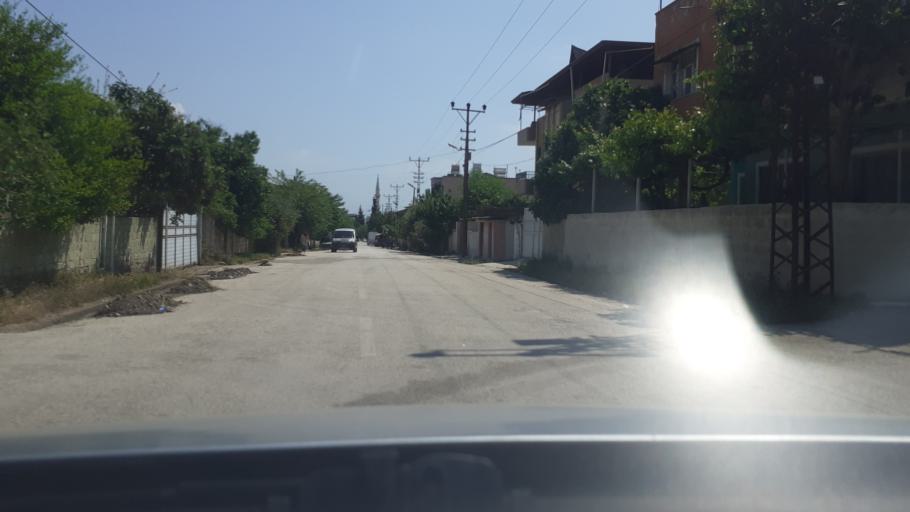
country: TR
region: Hatay
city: Kirikhan
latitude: 36.4900
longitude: 36.3540
